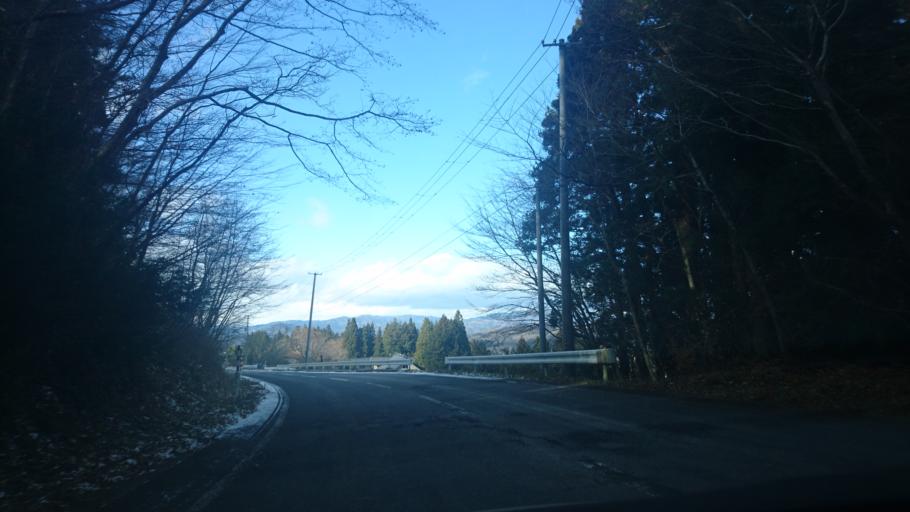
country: JP
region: Iwate
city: Ichinoseki
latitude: 38.9735
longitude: 141.3949
